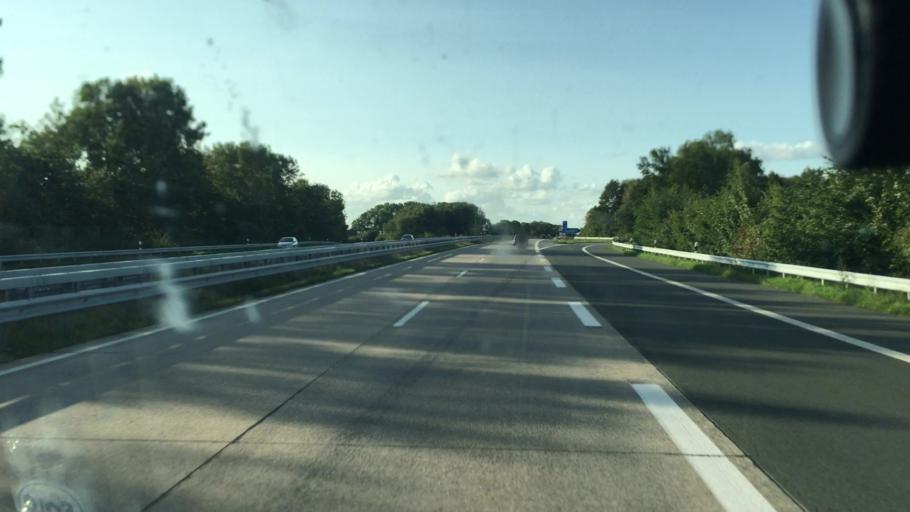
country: DE
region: Lower Saxony
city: Bockhorn
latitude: 53.4441
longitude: 8.0288
